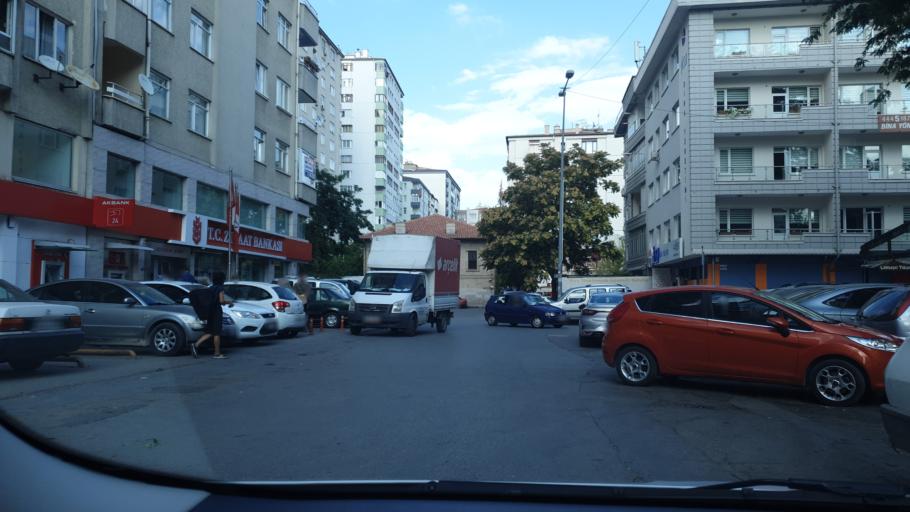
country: TR
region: Kayseri
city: Kayseri
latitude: 38.7236
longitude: 35.4930
